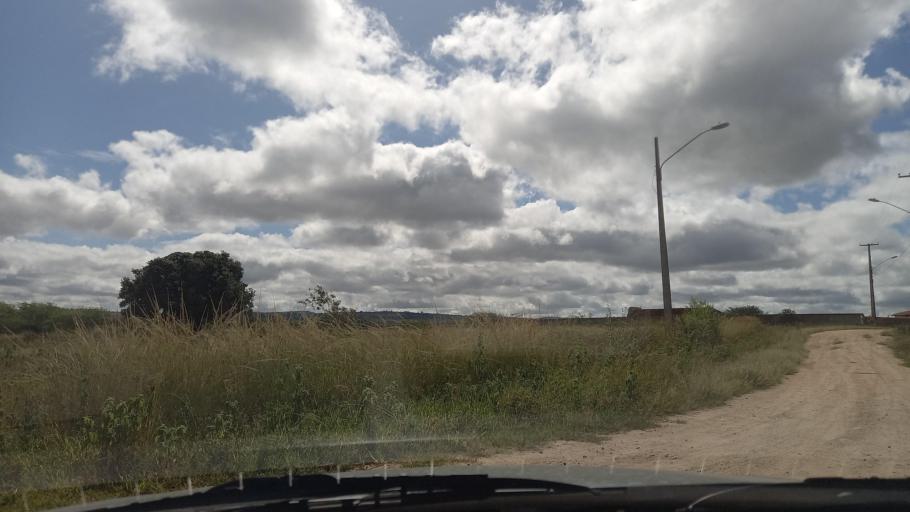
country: BR
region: Pernambuco
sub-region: Caruaru
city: Caruaru
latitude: -8.2321
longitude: -35.9846
